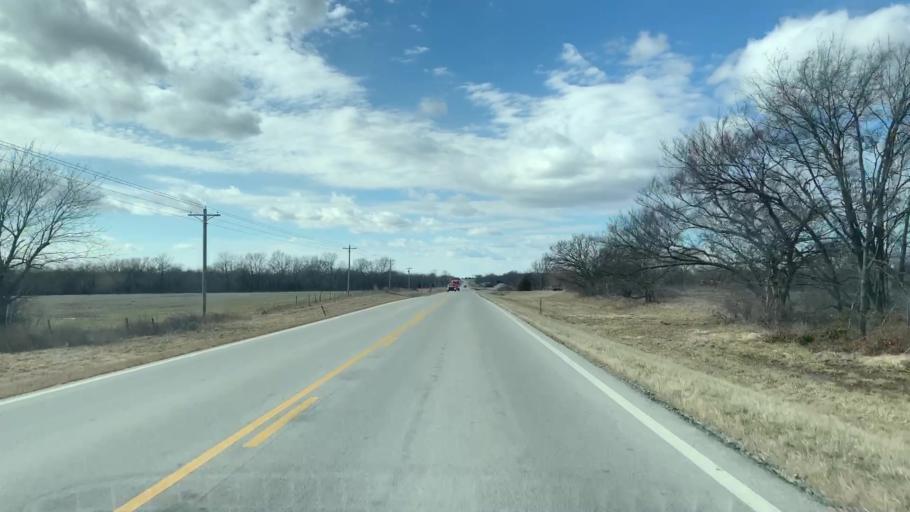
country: US
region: Kansas
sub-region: Neosho County
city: Erie
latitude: 37.5292
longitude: -95.2808
